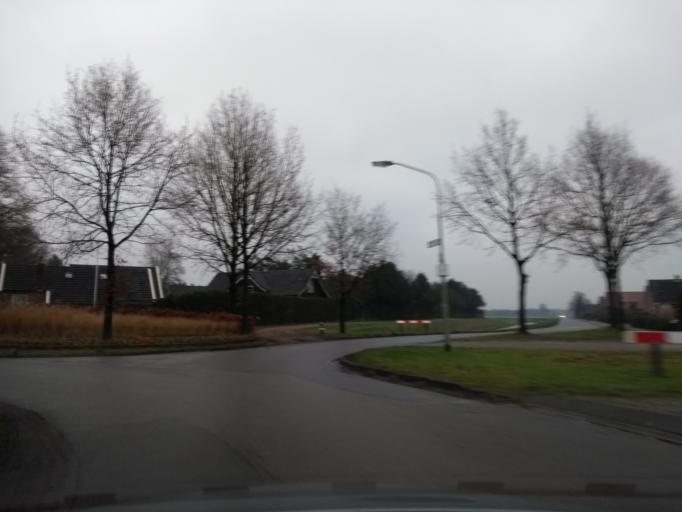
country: NL
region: Drenthe
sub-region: Gemeente Emmen
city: Klazienaveen
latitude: 52.7081
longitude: 6.9443
